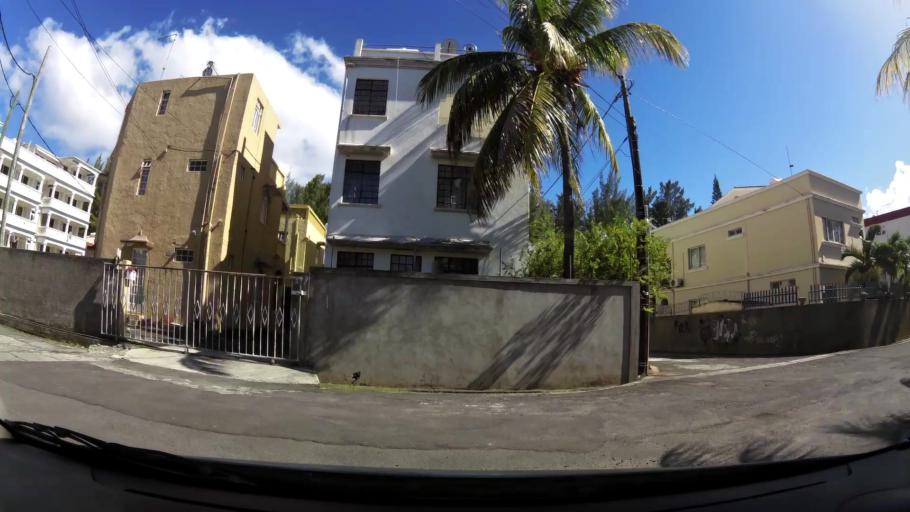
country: MU
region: Black River
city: Flic en Flac
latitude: -20.2919
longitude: 57.3645
